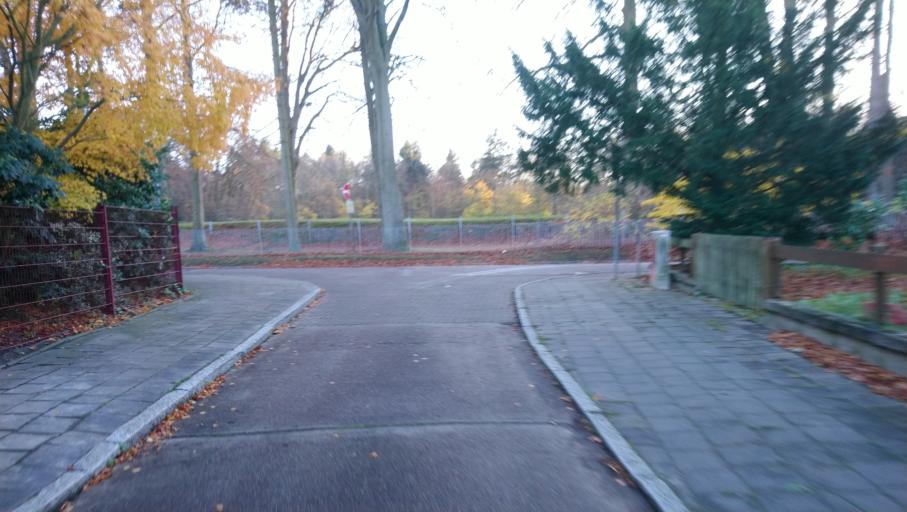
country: DE
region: Mecklenburg-Vorpommern
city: Kritzmow
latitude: 54.0832
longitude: 12.0819
